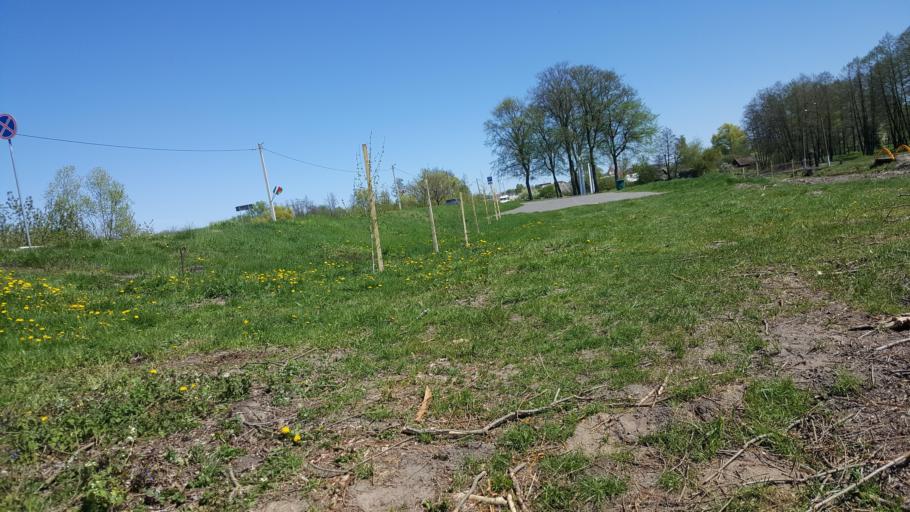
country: BY
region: Brest
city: Kamyanyets
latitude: 52.4016
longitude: 23.8040
